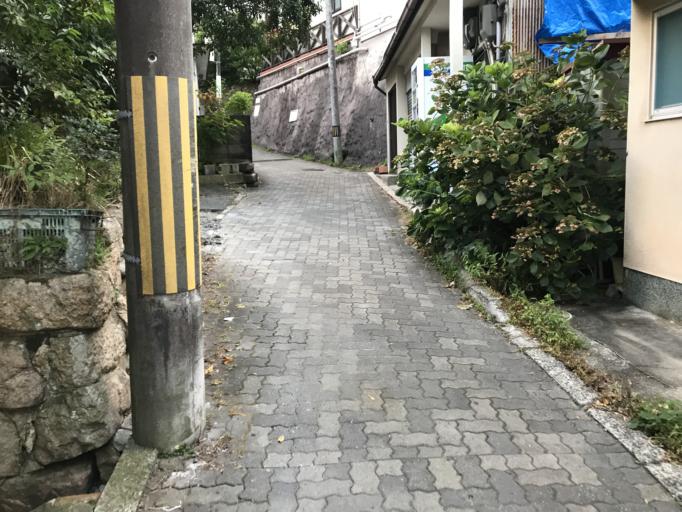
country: JP
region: Hyogo
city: Ashiya
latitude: 34.7957
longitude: 135.2494
